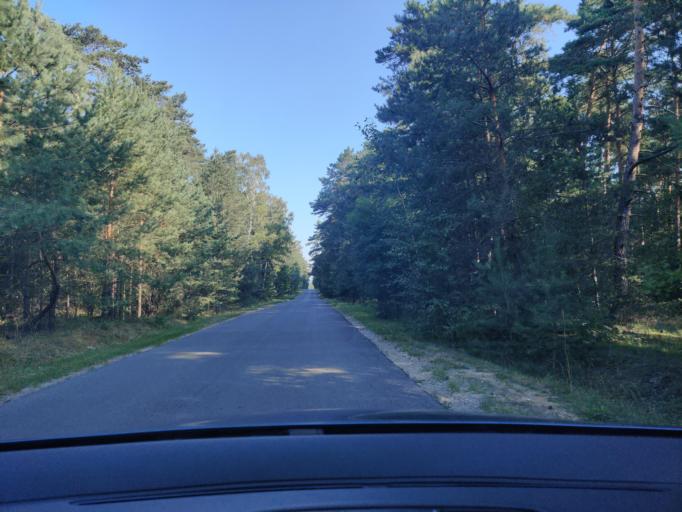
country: PL
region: Greater Poland Voivodeship
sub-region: Konin
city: Konin
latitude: 52.1788
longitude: 18.3354
